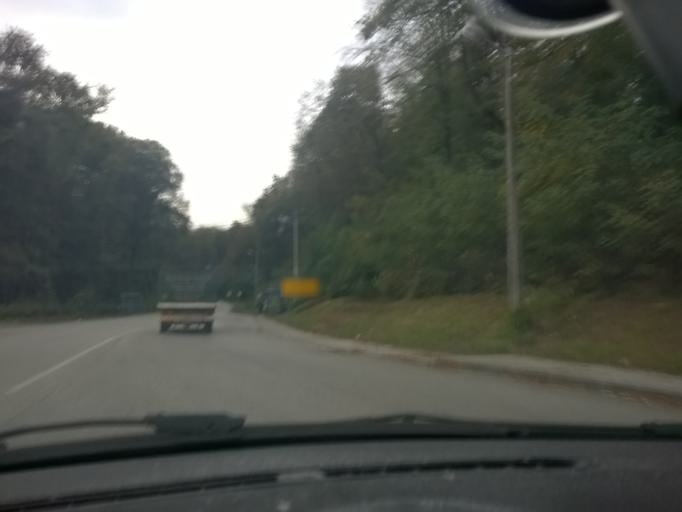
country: HR
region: Zagrebacka
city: Pojatno
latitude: 45.8917
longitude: 15.7950
